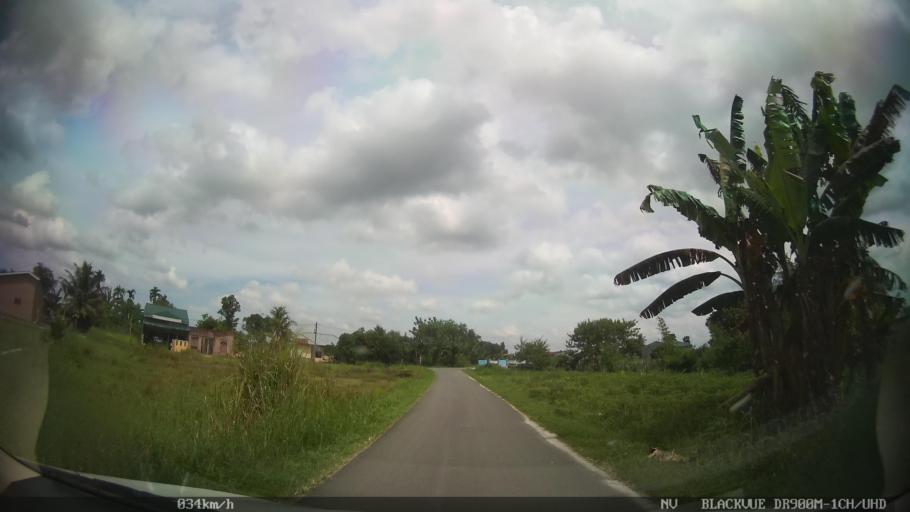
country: ID
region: North Sumatra
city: Percut
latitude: 3.5665
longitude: 98.8540
